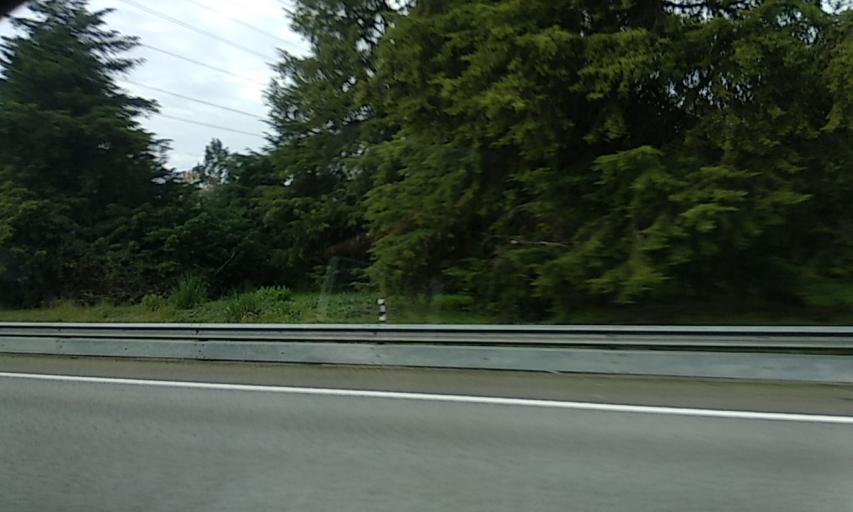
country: PT
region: Porto
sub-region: Valongo
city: Ermesinde
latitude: 41.2370
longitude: -8.5647
